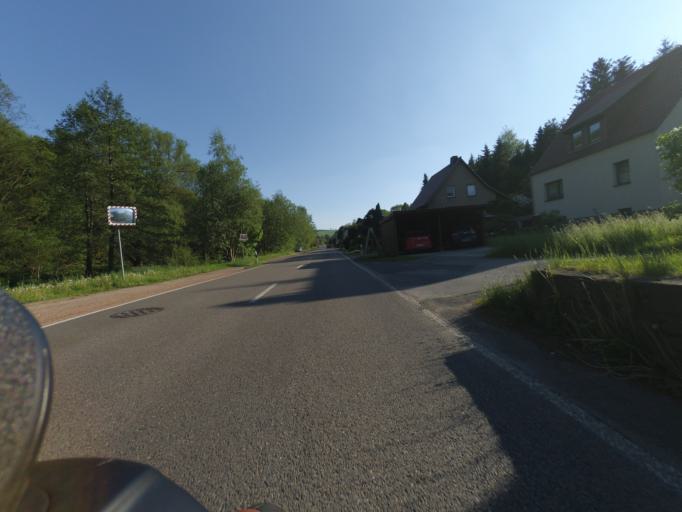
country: DE
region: Saxony
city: Dippoldiswalde
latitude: 50.8898
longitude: 13.6465
